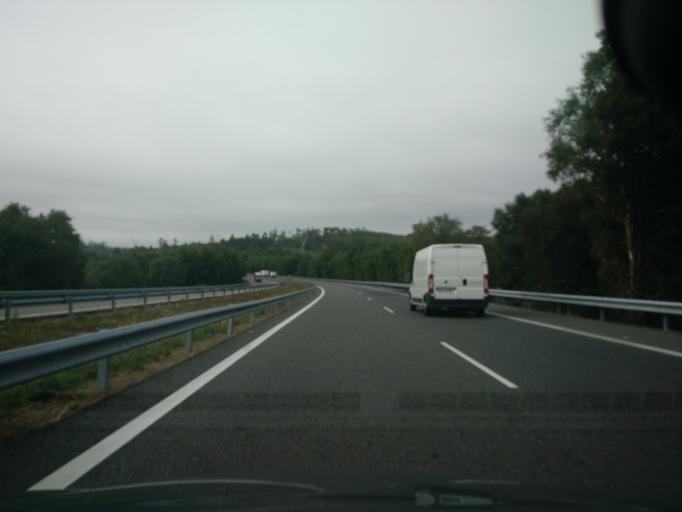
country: ES
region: Galicia
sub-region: Provincia da Coruna
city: Mesia
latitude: 43.1368
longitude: -8.3306
